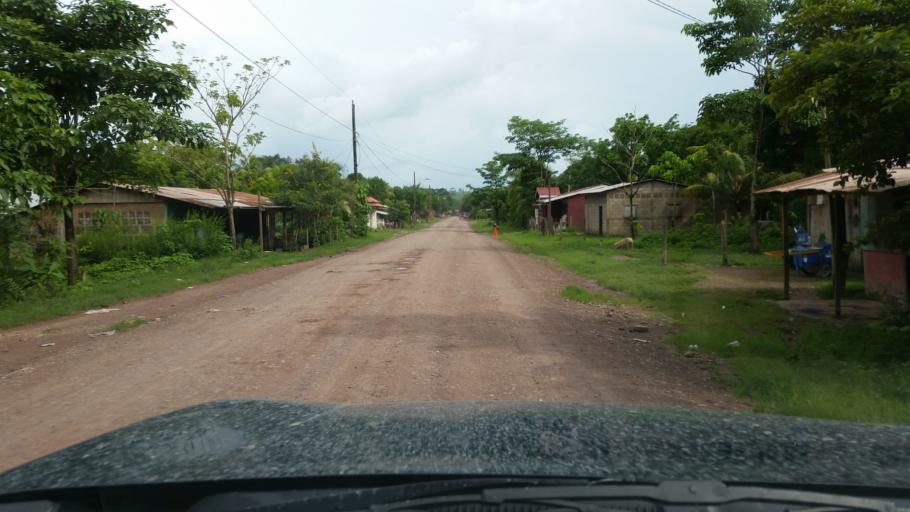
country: NI
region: Atlantico Norte (RAAN)
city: Siuna
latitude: 13.4831
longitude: -84.8444
